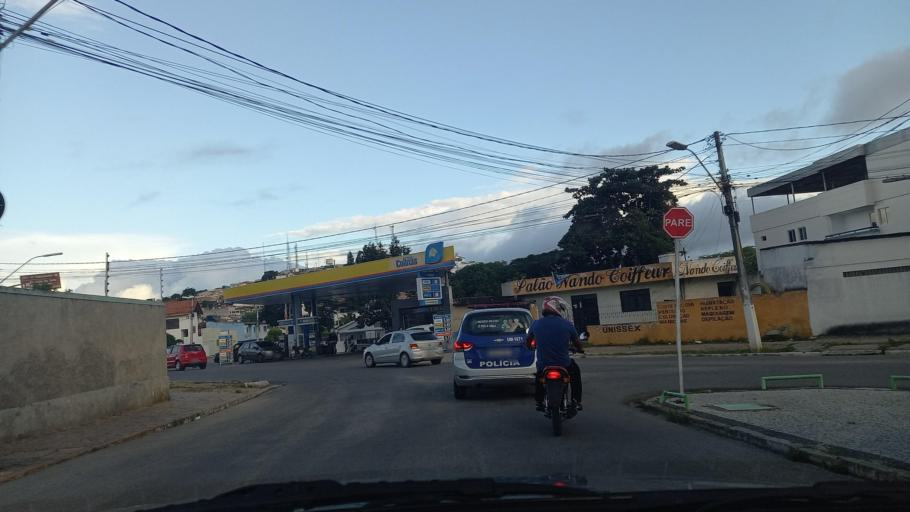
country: BR
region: Pernambuco
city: Garanhuns
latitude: -8.8828
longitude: -36.4746
